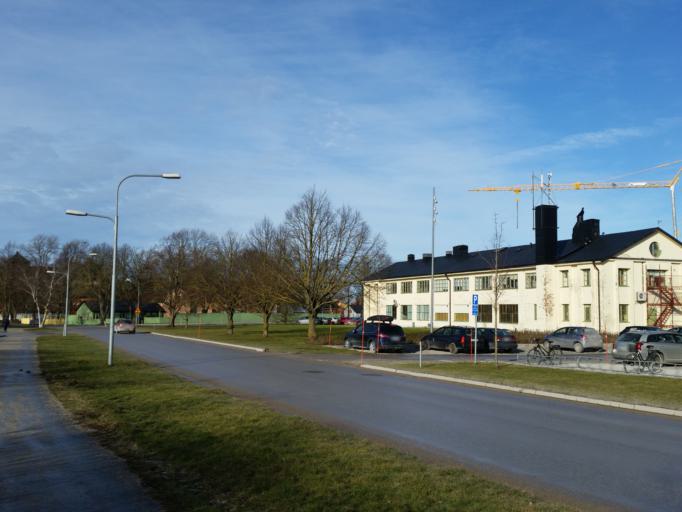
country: SE
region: Gotland
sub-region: Gotland
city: Visby
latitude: 57.6306
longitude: 18.3046
